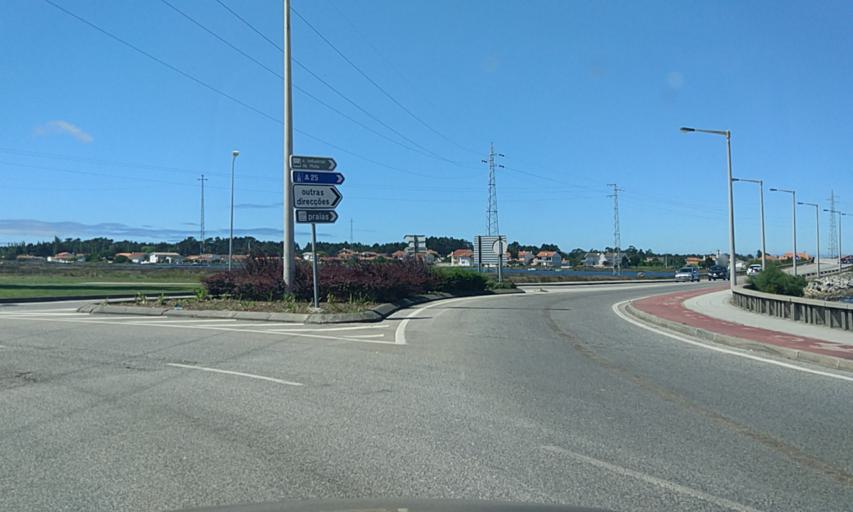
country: PT
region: Aveiro
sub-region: Ilhavo
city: Ilhavo
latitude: 40.6069
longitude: -8.6793
